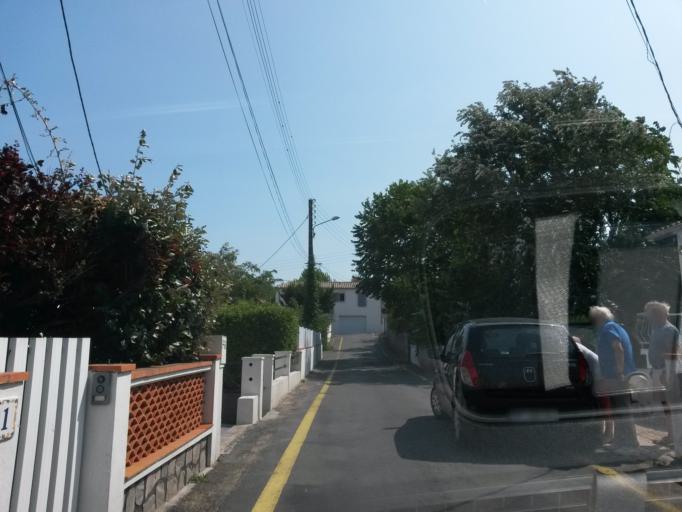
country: FR
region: Pays de la Loire
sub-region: Departement de la Vendee
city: La Tranche-sur-Mer
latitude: 46.3414
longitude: -1.4401
